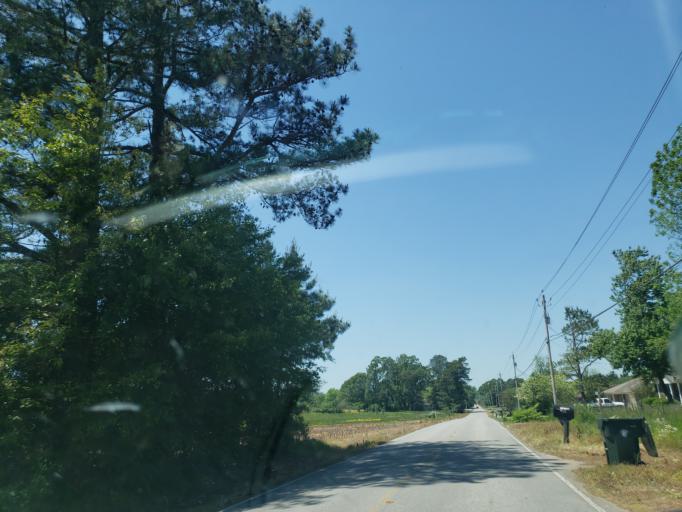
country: US
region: Alabama
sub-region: Madison County
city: Harvest
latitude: 34.9624
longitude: -86.7048
